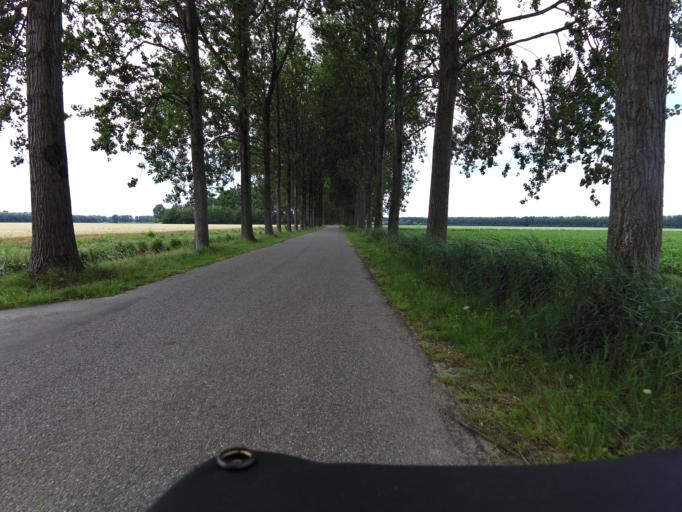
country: NL
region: North Brabant
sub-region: Gemeente Moerdijk
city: Willemstad
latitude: 51.7176
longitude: 4.4931
